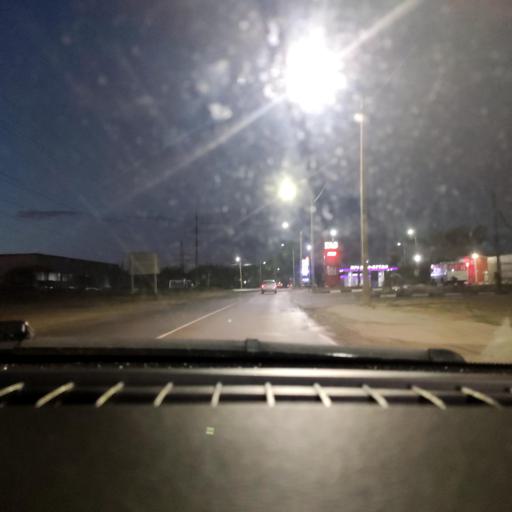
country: RU
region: Voronezj
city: Maslovka
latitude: 51.5938
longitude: 39.2485
